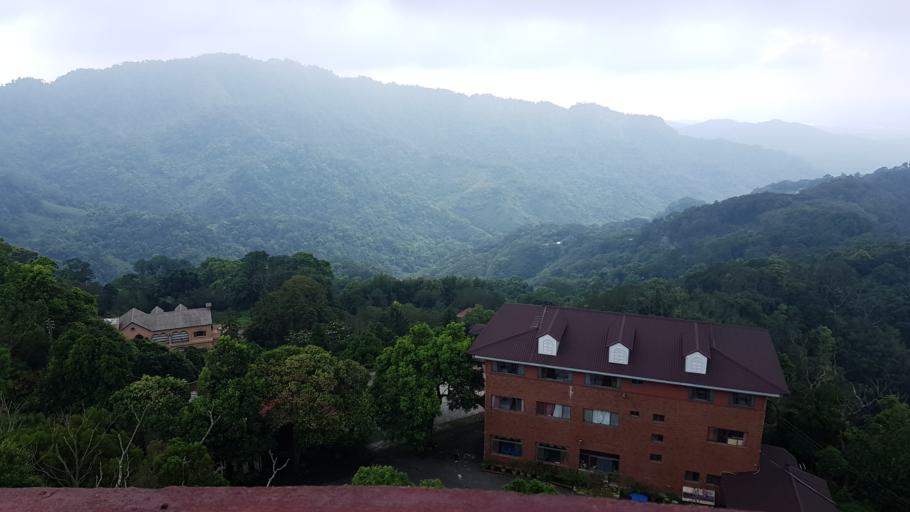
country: TW
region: Taiwan
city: Fengyuan
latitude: 24.3890
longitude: 120.8227
